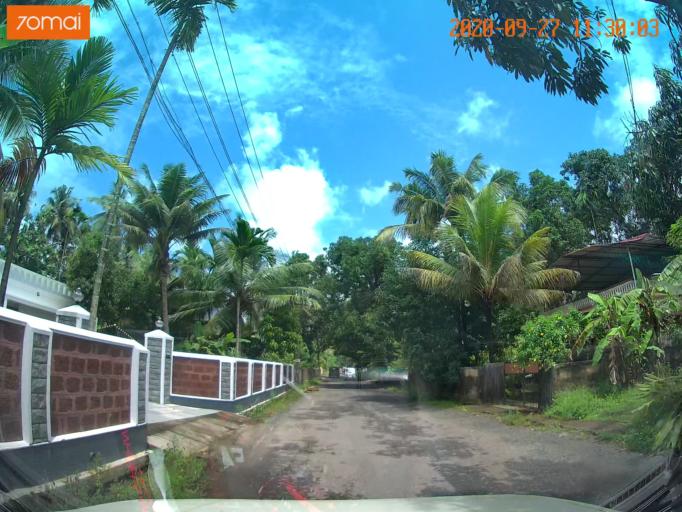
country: IN
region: Kerala
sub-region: Thrissur District
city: Thanniyam
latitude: 10.4181
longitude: 76.1344
